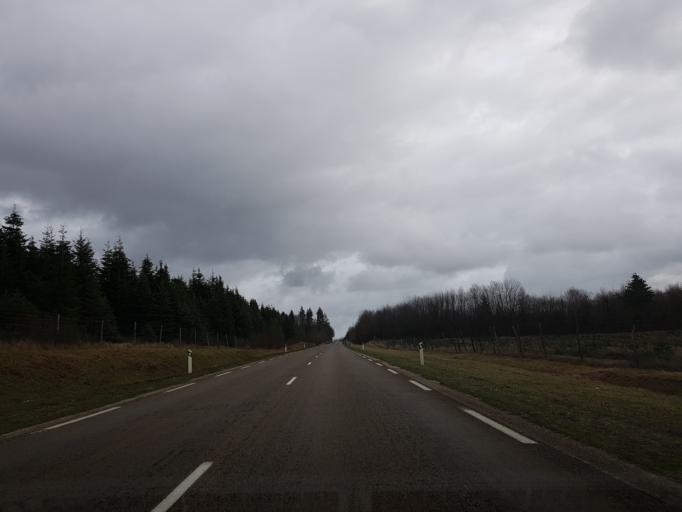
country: FR
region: Franche-Comte
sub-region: Departement de la Haute-Saone
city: Scey-sur-Saone-et-Saint-Albin
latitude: 47.6989
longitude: 5.9538
